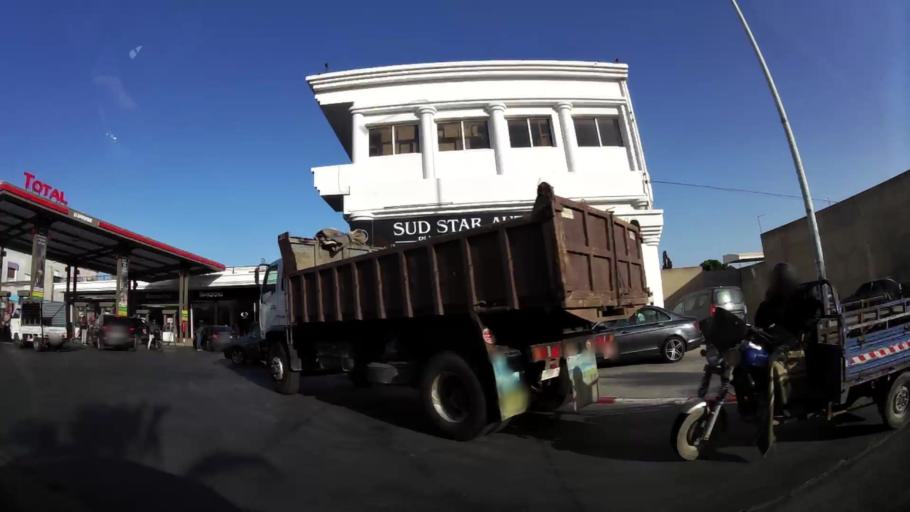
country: MA
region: Oued ed Dahab-Lagouira
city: Dakhla
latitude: 30.4105
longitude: -9.5478
